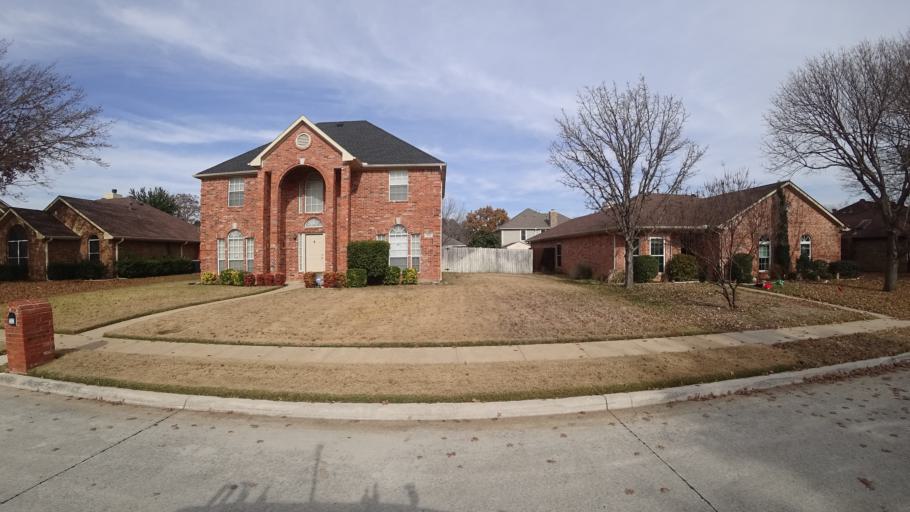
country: US
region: Texas
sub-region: Denton County
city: Highland Village
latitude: 33.0794
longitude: -97.0285
